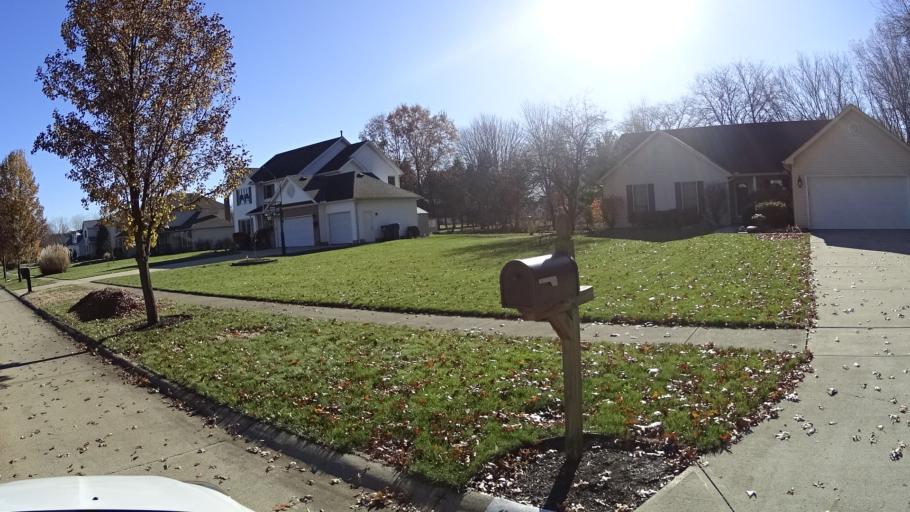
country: US
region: Ohio
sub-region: Lorain County
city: Avon Center
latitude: 41.4370
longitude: -82.0087
